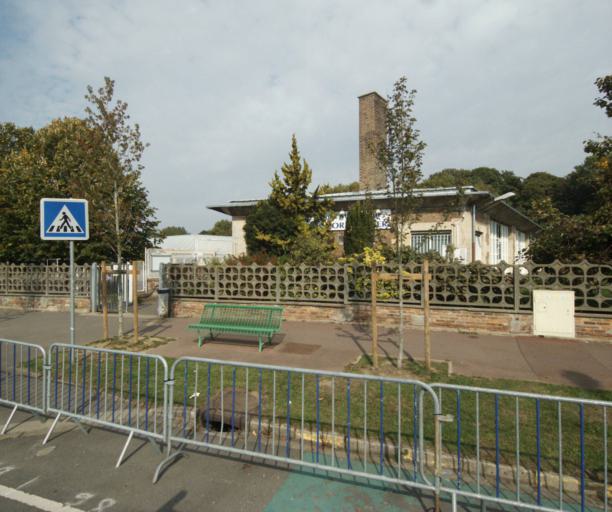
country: FR
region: Nord-Pas-de-Calais
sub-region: Departement du Nord
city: Haubourdin
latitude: 50.6128
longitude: 2.9937
